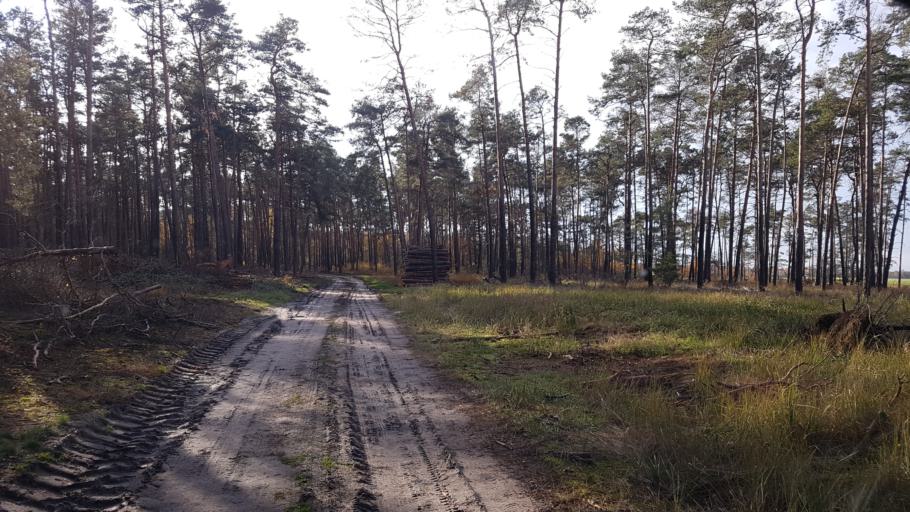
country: DE
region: Brandenburg
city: Trobitz
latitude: 51.6507
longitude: 13.4209
